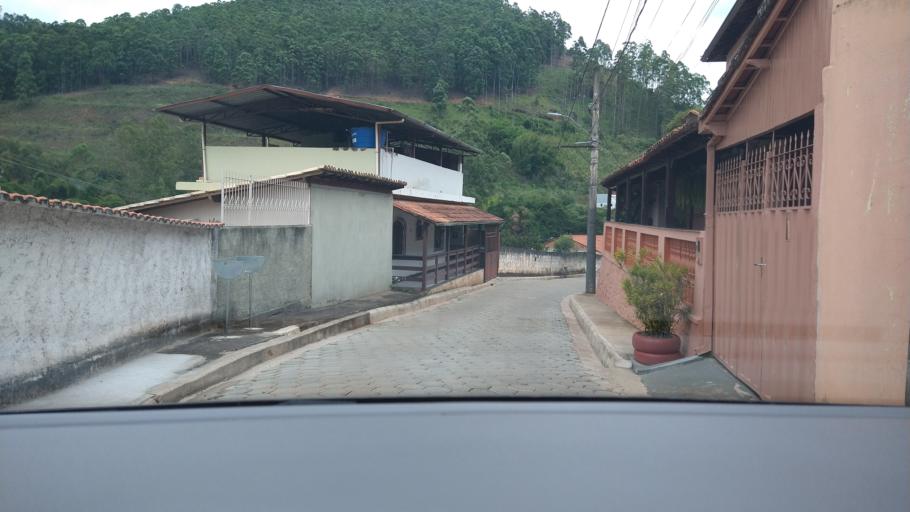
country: BR
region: Minas Gerais
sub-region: Rio Piracicaba
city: Rio Piracicaba
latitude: -19.9366
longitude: -43.1764
